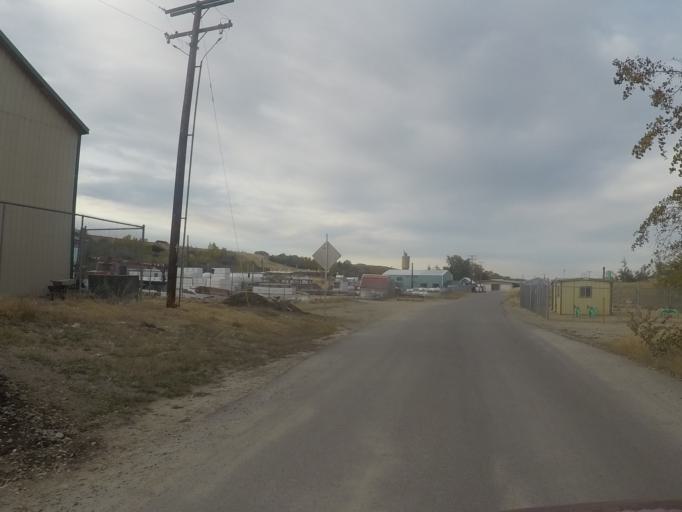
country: US
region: Montana
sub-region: Carbon County
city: Red Lodge
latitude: 45.1971
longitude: -109.2447
